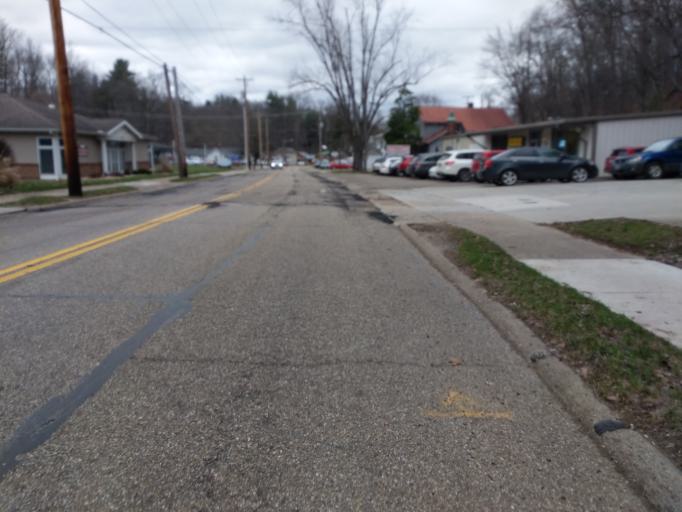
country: US
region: Ohio
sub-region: Athens County
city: Athens
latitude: 39.3071
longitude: -82.1040
